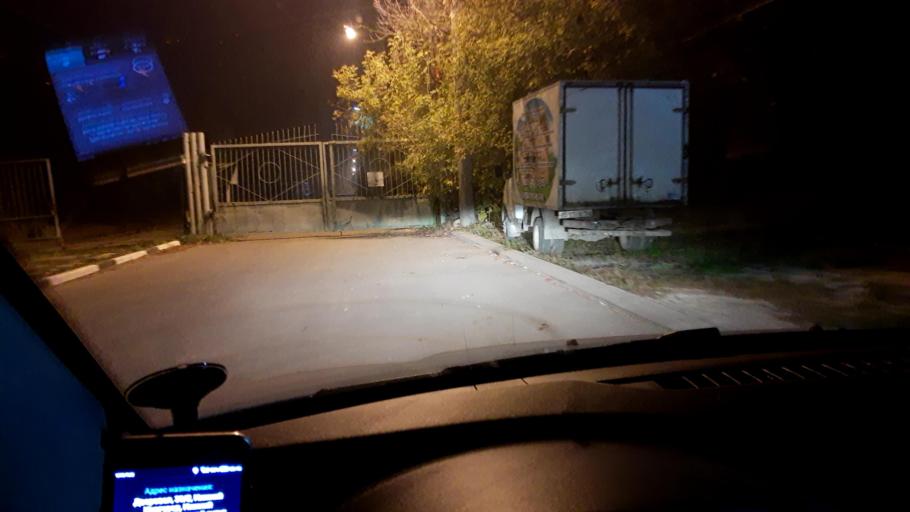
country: RU
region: Nizjnij Novgorod
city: Gorbatovka
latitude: 56.2445
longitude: 43.8234
